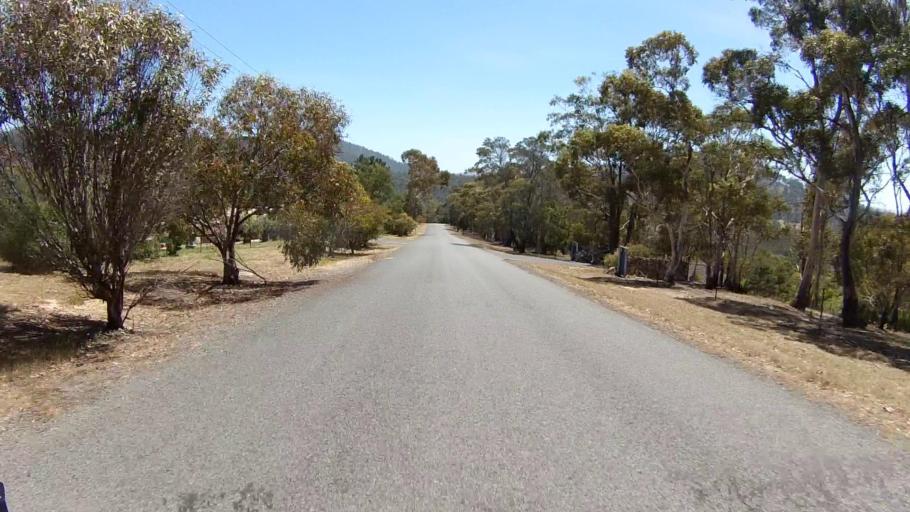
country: AU
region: Tasmania
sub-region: Clarence
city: Cambridge
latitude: -42.8470
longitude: 147.4240
